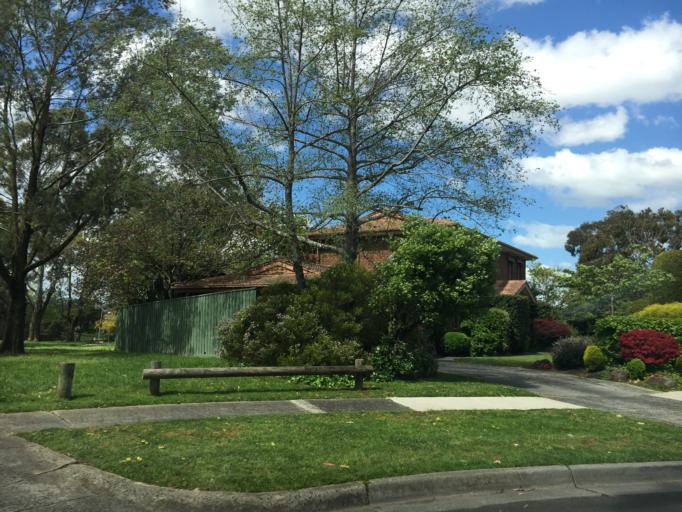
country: AU
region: Victoria
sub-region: Whitehorse
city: Vermont South
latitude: -37.8863
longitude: 145.1843
